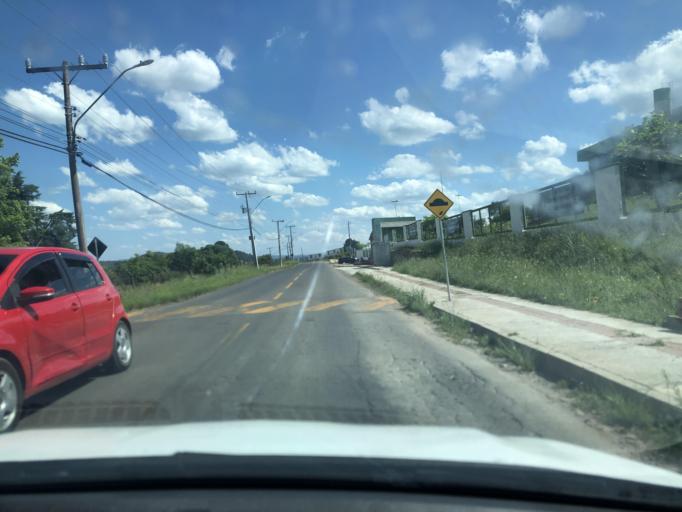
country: BR
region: Santa Catarina
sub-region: Lages
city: Lages
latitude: -27.8044
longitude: -50.3368
